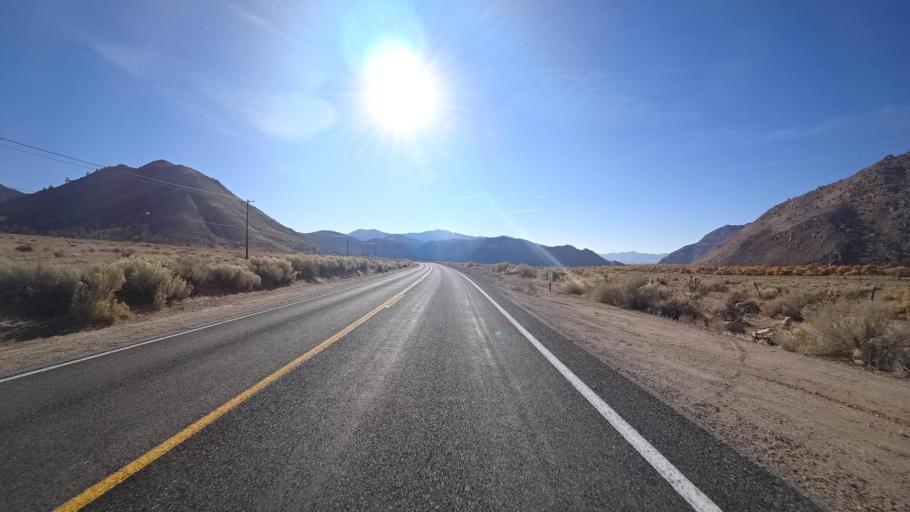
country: US
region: California
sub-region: Kern County
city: Weldon
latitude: 35.7105
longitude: -118.1766
